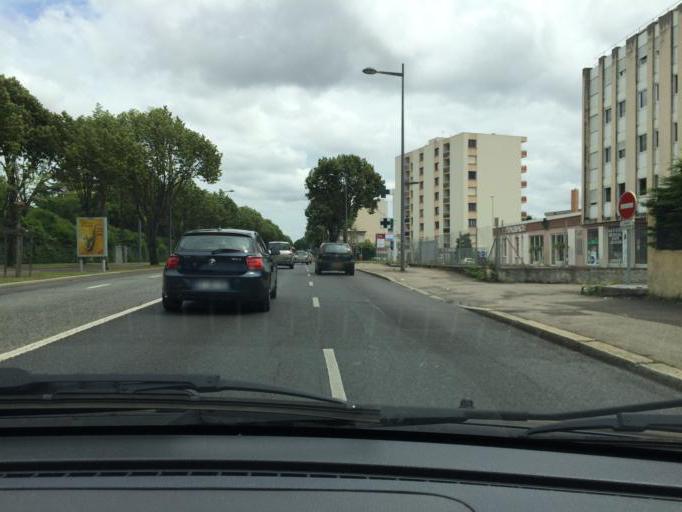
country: FR
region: Rhone-Alpes
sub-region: Departement du Rhone
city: Bron
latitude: 45.7380
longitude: 4.8954
